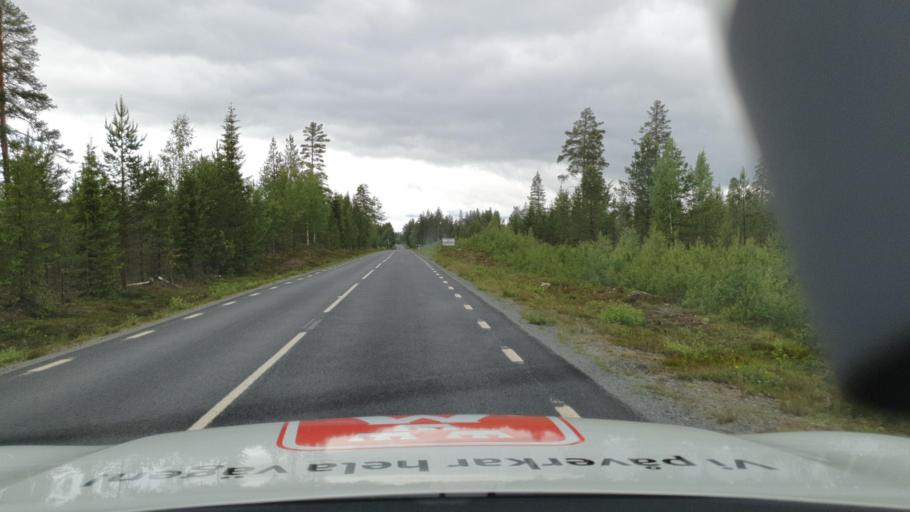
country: SE
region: Vaesterbotten
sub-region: Dorotea Kommun
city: Dorotea
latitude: 64.2101
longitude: 16.5564
